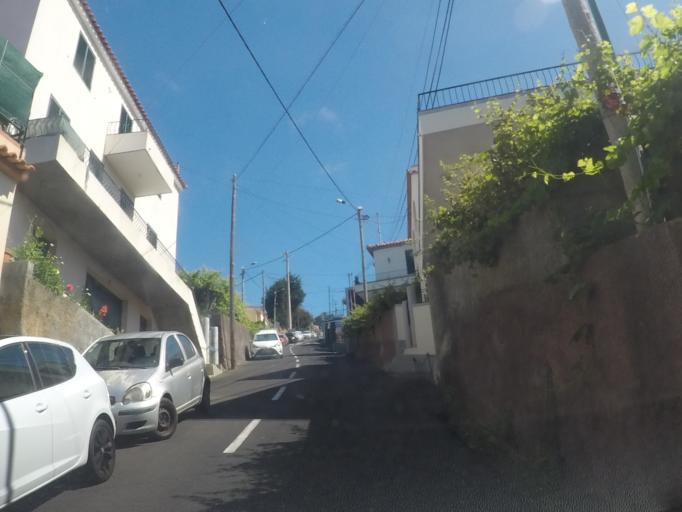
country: PT
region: Madeira
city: Camara de Lobos
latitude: 32.6711
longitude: -16.9649
